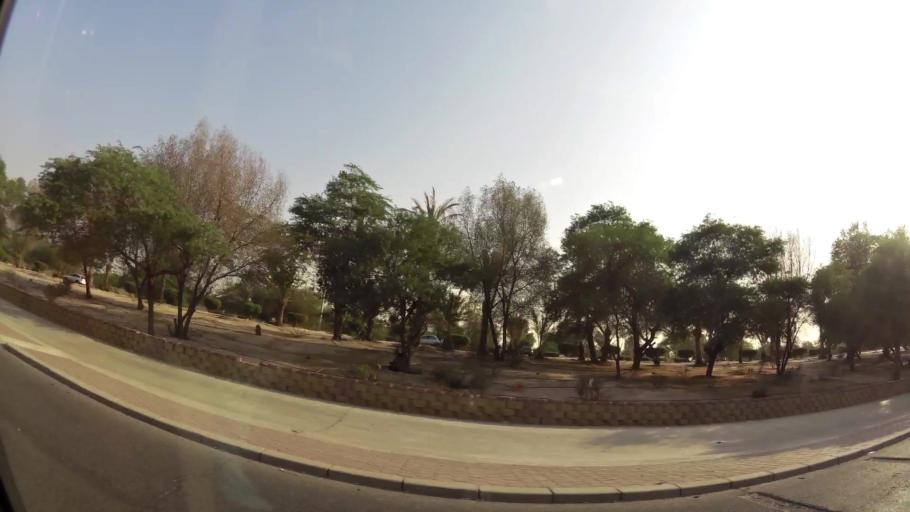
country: KW
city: Bayan
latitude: 29.3078
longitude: 48.0267
